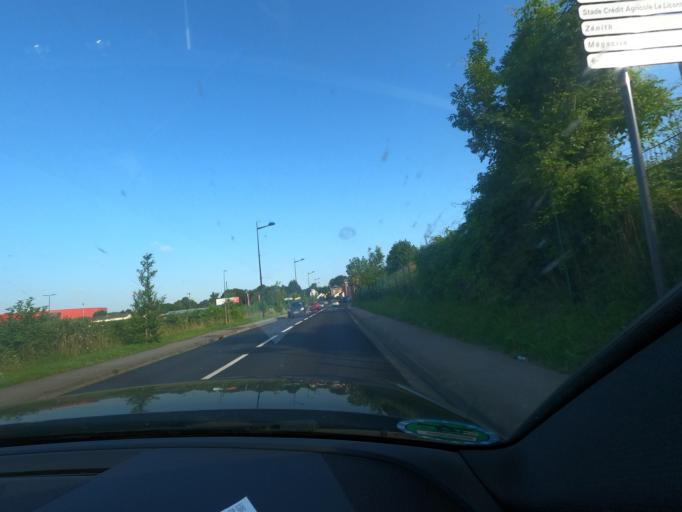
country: FR
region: Picardie
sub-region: Departement de la Somme
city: Amiens
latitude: 49.8959
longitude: 2.2742
